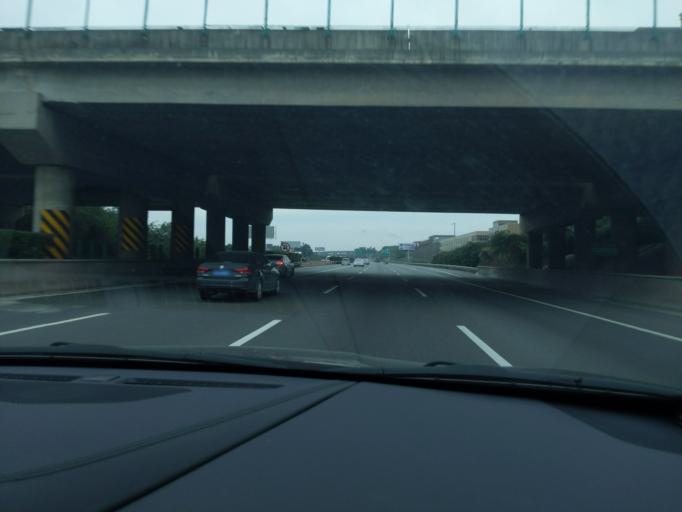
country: CN
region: Fujian
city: Neikeng
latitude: 24.7812
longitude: 118.4675
